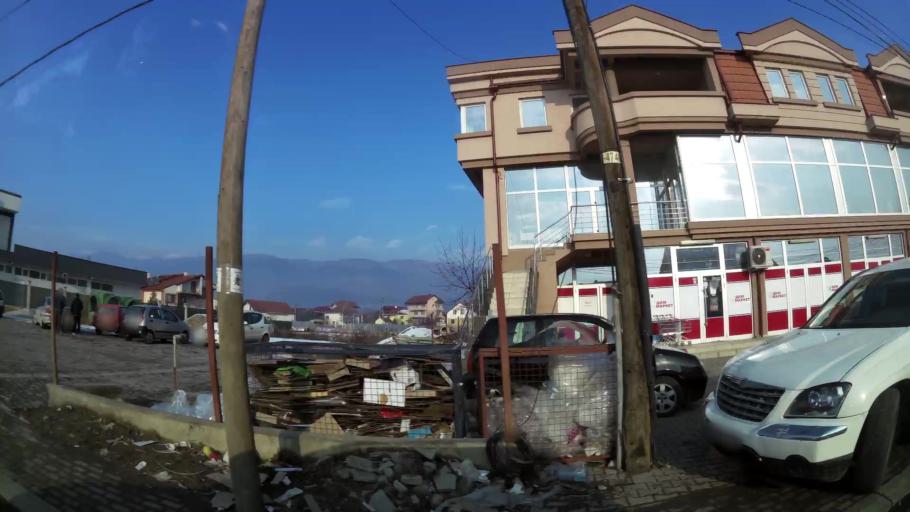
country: MK
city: Creshevo
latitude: 42.0263
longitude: 21.5146
